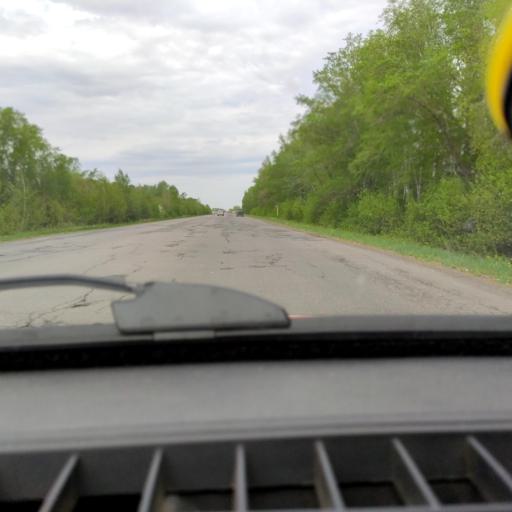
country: RU
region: Samara
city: Tol'yatti
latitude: 53.6504
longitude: 49.4230
